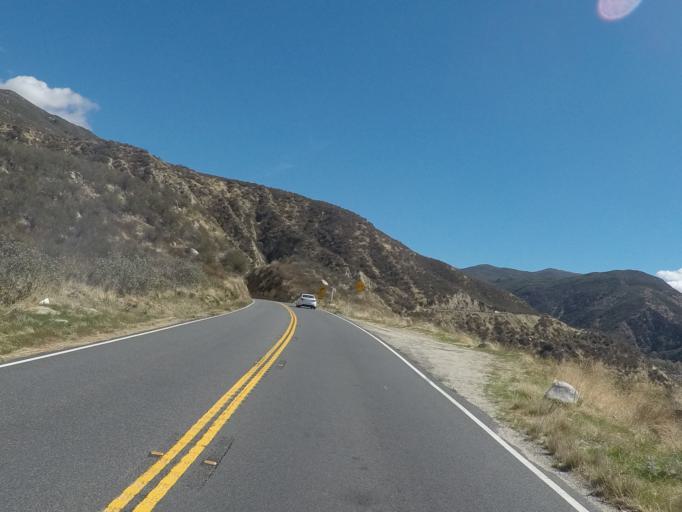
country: US
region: California
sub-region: Riverside County
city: Idyllwild-Pine Cove
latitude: 33.7178
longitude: -116.7908
